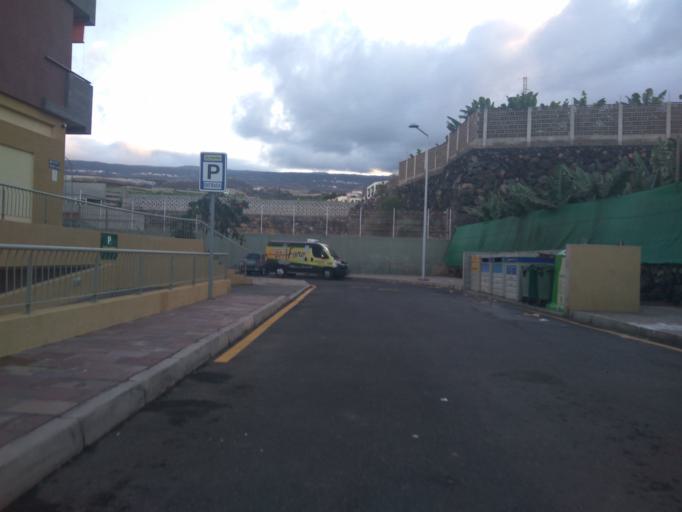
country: ES
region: Canary Islands
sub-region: Provincia de Santa Cruz de Tenerife
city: Guia de Isora
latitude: 28.2008
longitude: -16.8257
